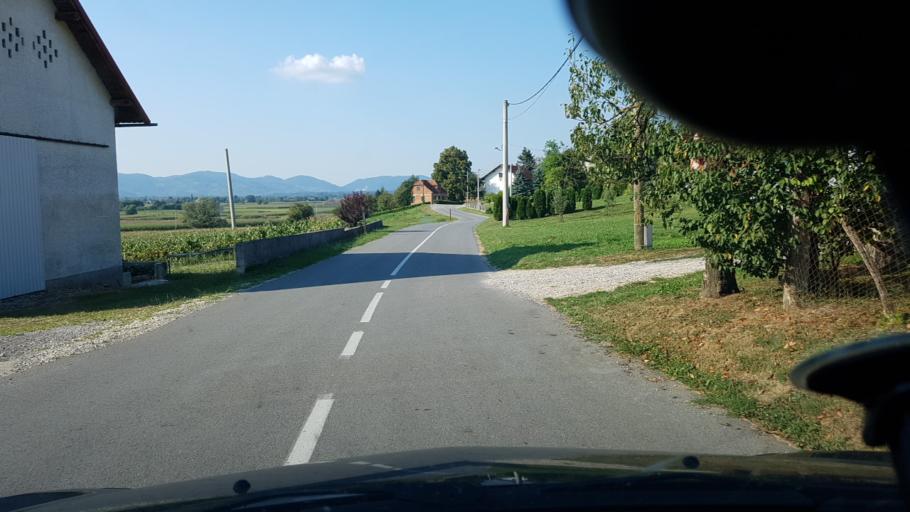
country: HR
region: Zagrebacka
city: Pojatno
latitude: 45.9374
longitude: 15.7275
